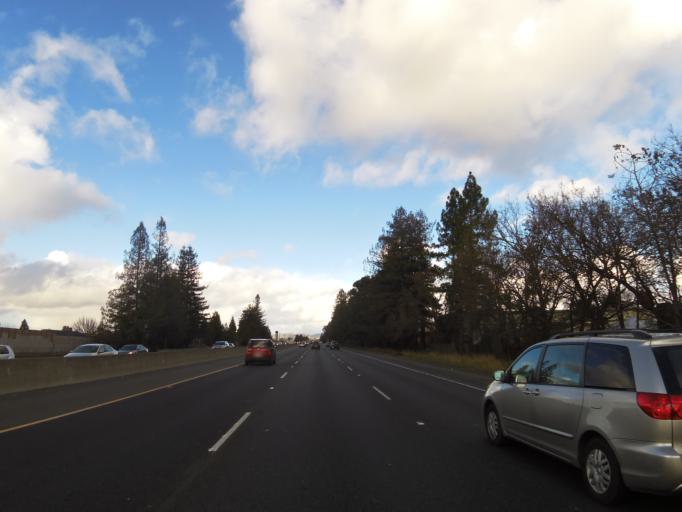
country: US
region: California
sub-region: Sonoma County
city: Roseland
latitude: 38.3966
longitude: -122.7160
